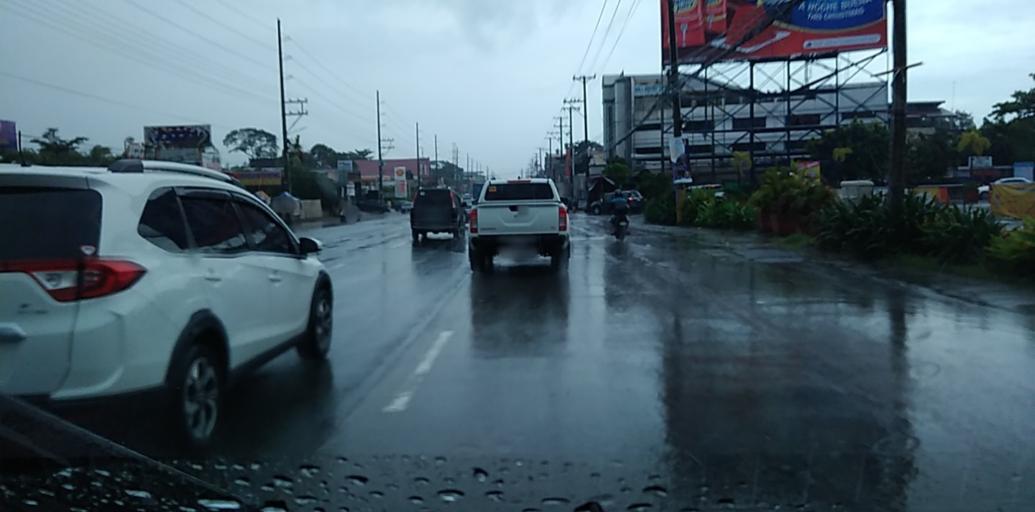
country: PH
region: Central Luzon
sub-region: Province of Pampanga
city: Magliman
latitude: 15.0488
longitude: 120.6666
